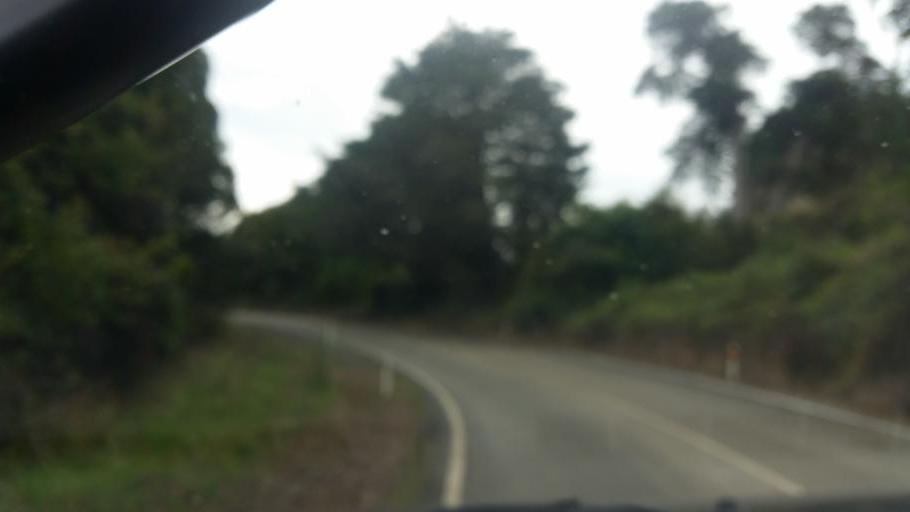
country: NZ
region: Northland
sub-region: Kaipara District
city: Dargaville
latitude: -35.7495
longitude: 173.9050
